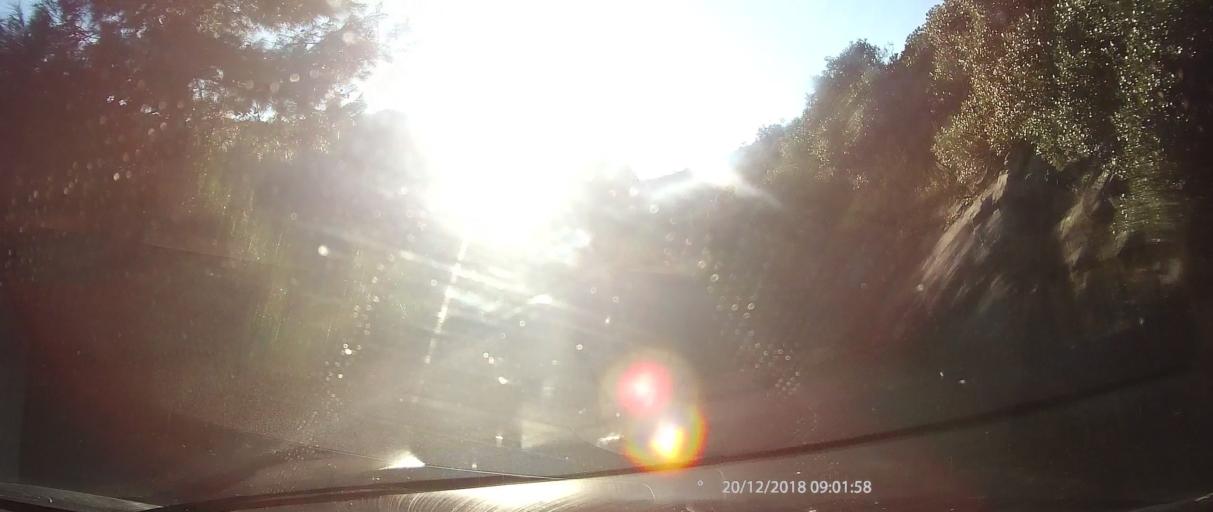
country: GR
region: Peloponnese
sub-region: Nomos Lakonias
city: Sykea
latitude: 36.9568
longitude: 22.9900
